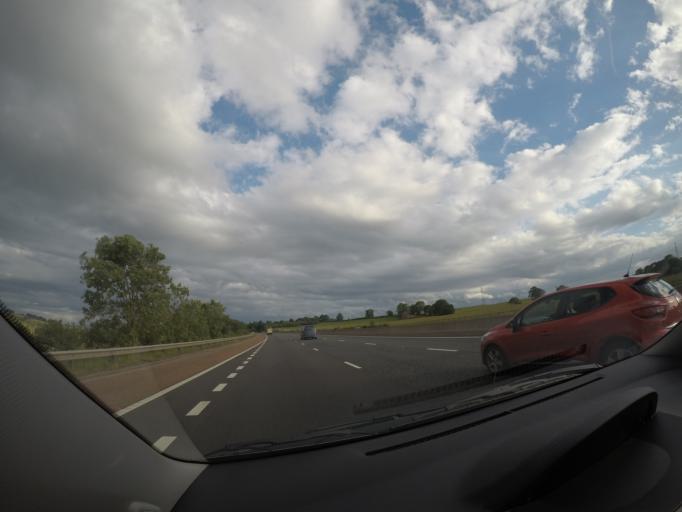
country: GB
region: England
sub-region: Cumbria
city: Penrith
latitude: 54.6876
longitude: -2.7906
